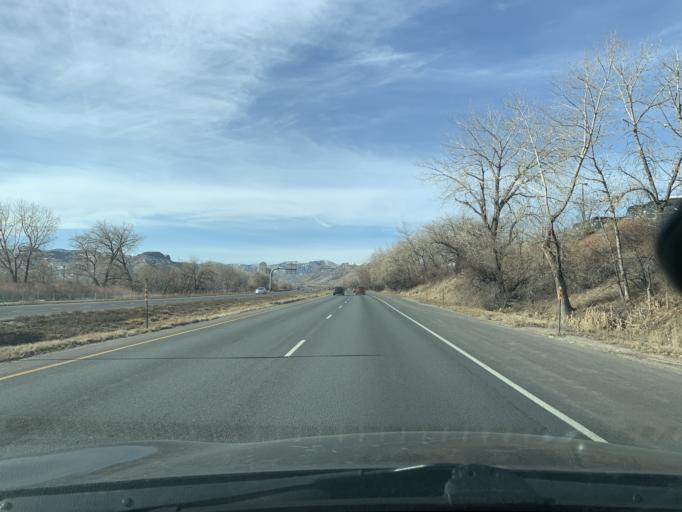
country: US
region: Colorado
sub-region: Jefferson County
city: Applewood
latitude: 39.7751
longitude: -105.1574
